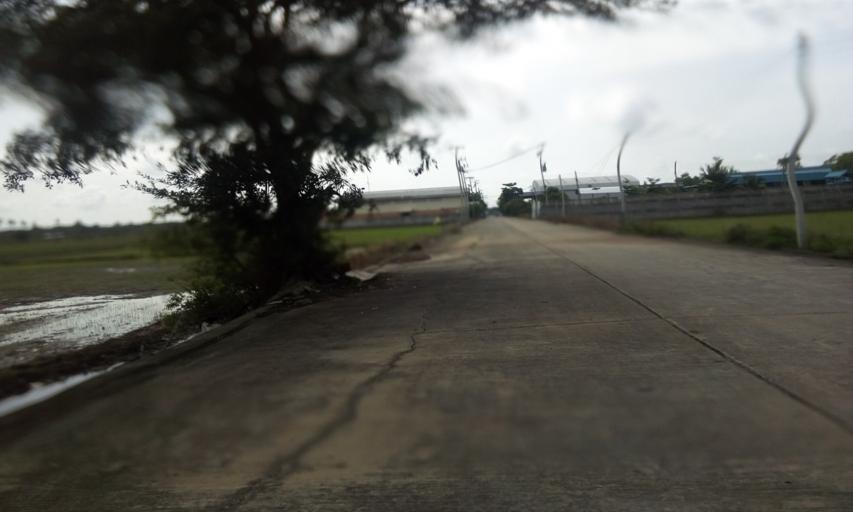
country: TH
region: Pathum Thani
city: Ban Lam Luk Ka
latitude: 13.9869
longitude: 100.8349
